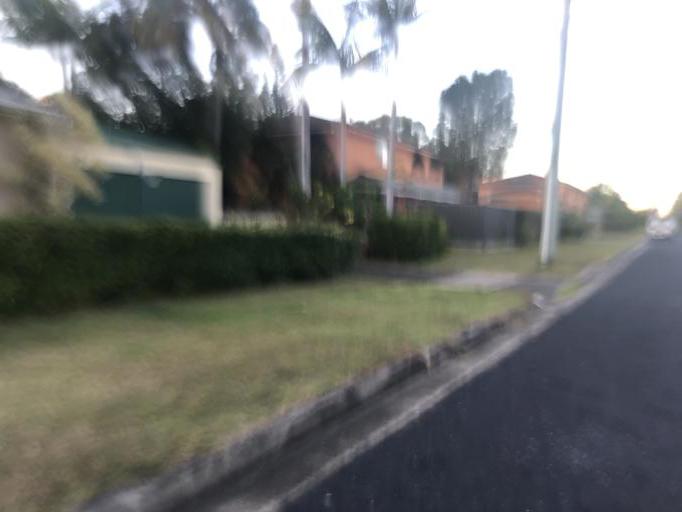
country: AU
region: New South Wales
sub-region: Coffs Harbour
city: Coffs Harbour
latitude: -30.2867
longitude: 153.1358
